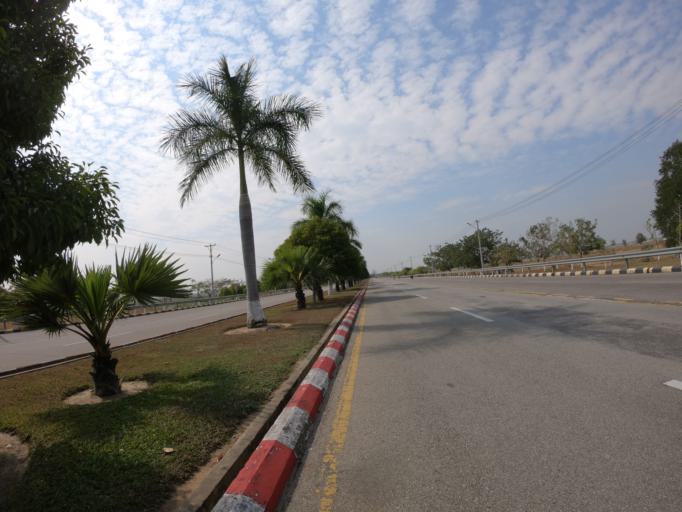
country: MM
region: Mandalay
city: Pyinmana
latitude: 19.6059
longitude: 96.1816
